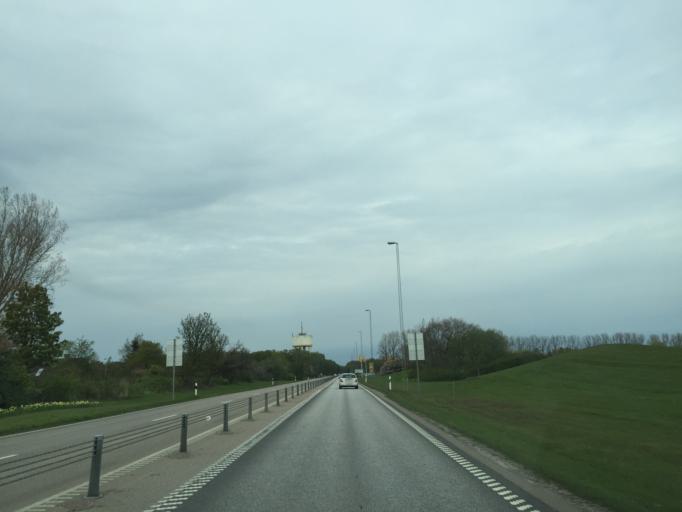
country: SE
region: Skane
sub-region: Hoganas Kommun
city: Hoganas
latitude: 56.1776
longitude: 12.5631
